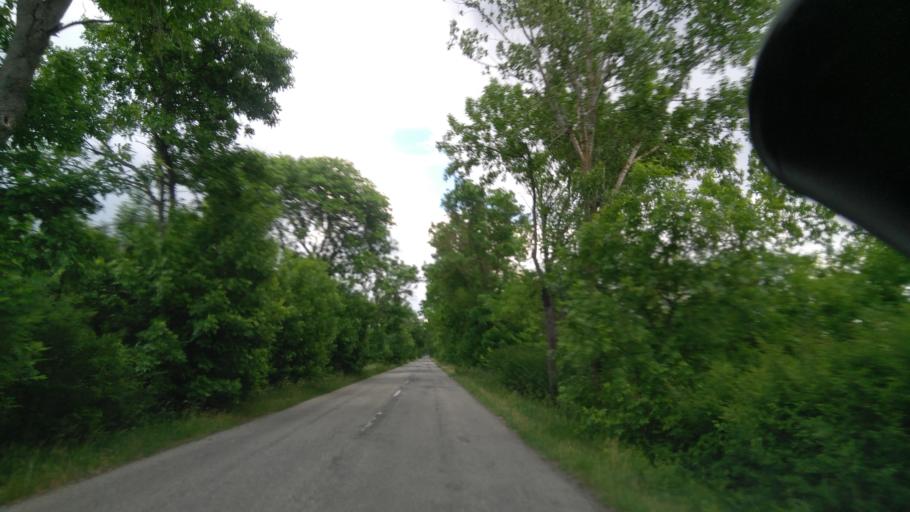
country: HU
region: Bekes
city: Bucsa
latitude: 47.1628
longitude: 21.0929
